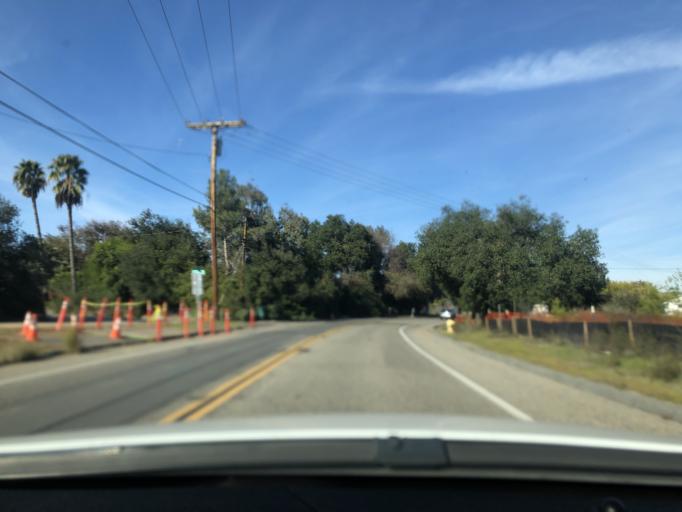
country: US
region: California
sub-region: San Diego County
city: Escondido
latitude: 33.0883
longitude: -117.0848
